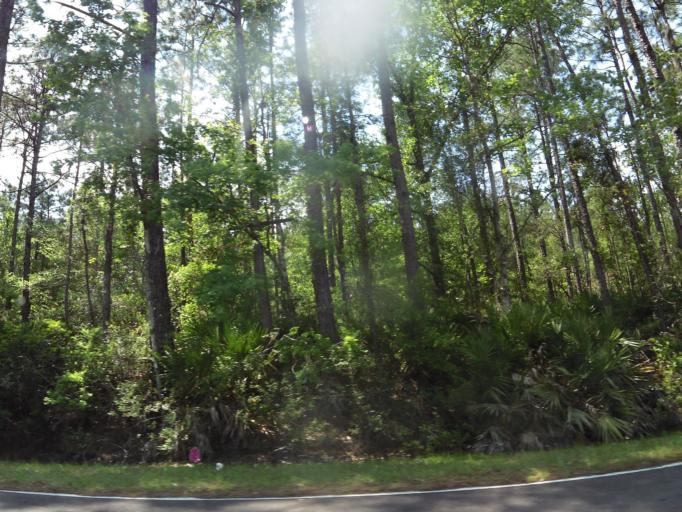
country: US
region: Florida
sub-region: Nassau County
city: Yulee
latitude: 30.5160
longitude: -81.6603
